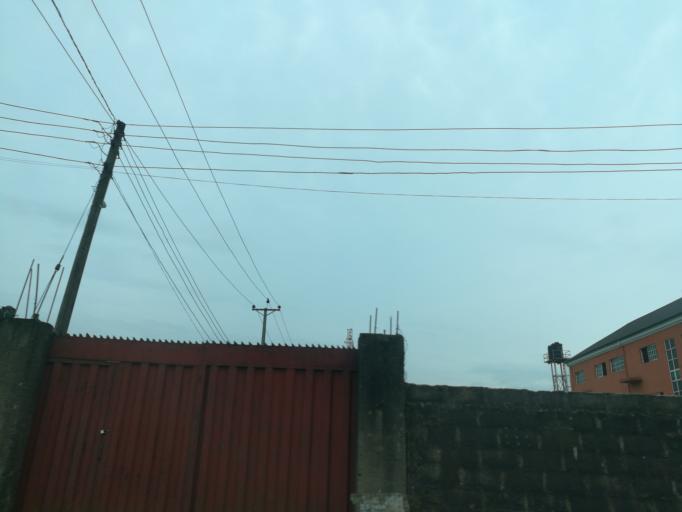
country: NG
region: Rivers
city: Port Harcourt
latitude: 4.8297
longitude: 7.0172
